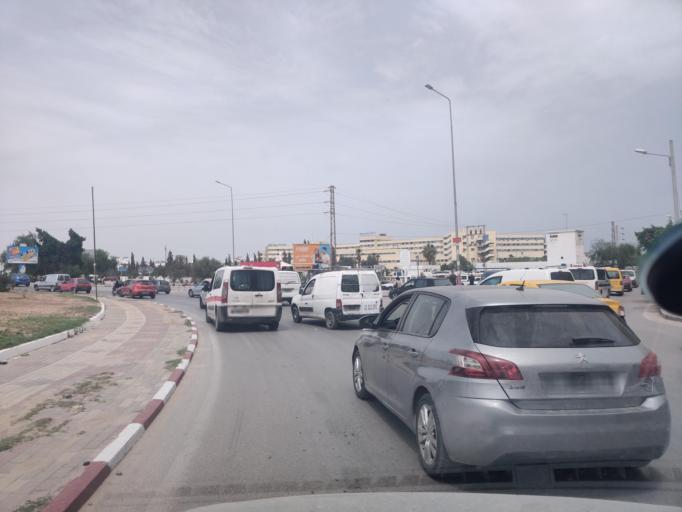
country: TN
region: Susah
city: Hammam Sousse
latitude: 35.8335
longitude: 10.5900
